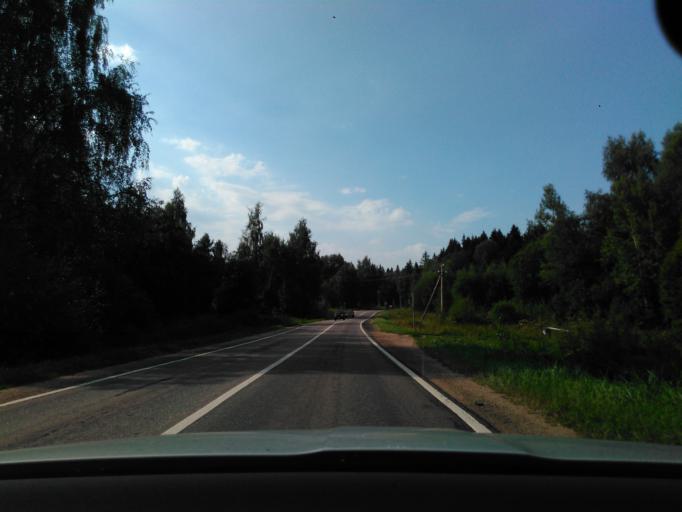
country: RU
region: Moskovskaya
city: Solnechnogorsk
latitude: 56.1431
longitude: 36.8319
